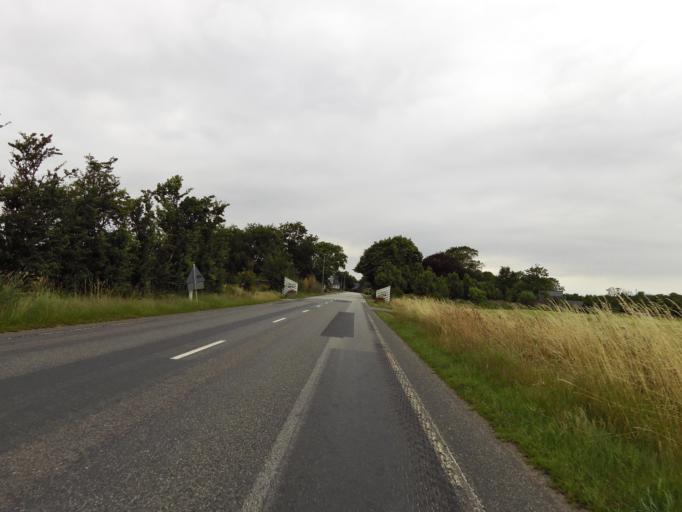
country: DK
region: South Denmark
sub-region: Tonder Kommune
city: Logumkloster
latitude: 55.1466
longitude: 8.9625
